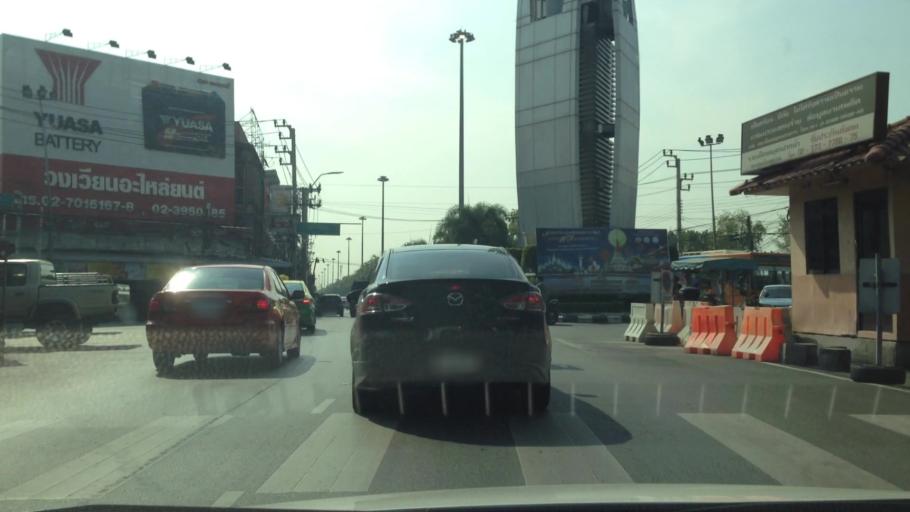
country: TH
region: Samut Prakan
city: Samut Prakan
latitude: 13.5910
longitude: 100.5970
